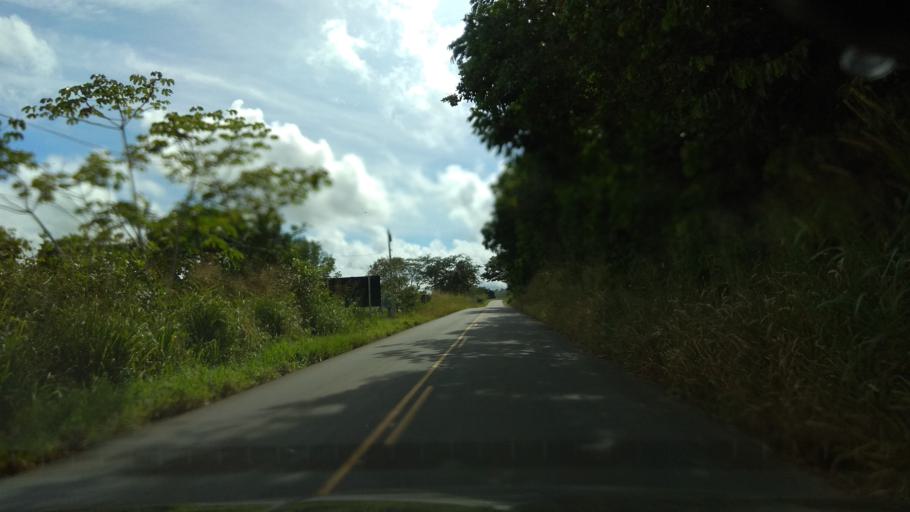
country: BR
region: Bahia
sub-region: Mutuipe
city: Mutuipe
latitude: -13.1995
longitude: -39.4632
